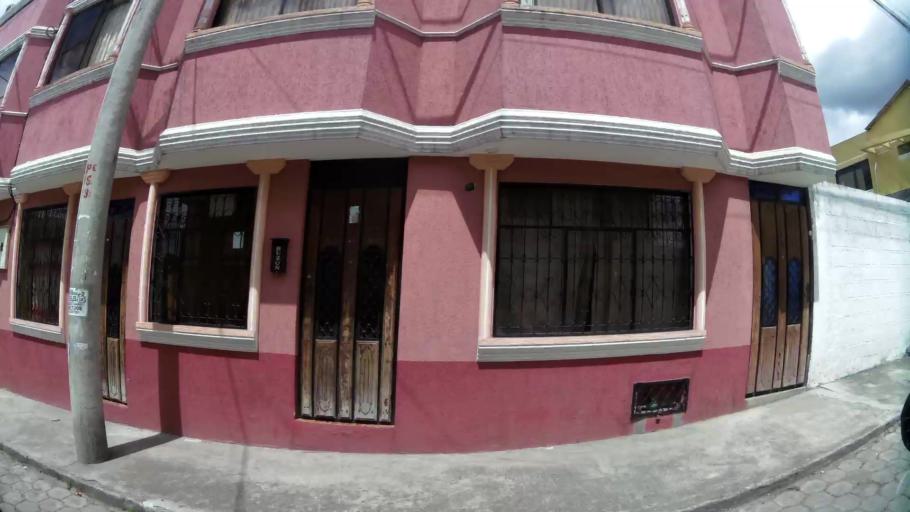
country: EC
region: Pichincha
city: Sangolqui
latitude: -0.3399
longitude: -78.5449
